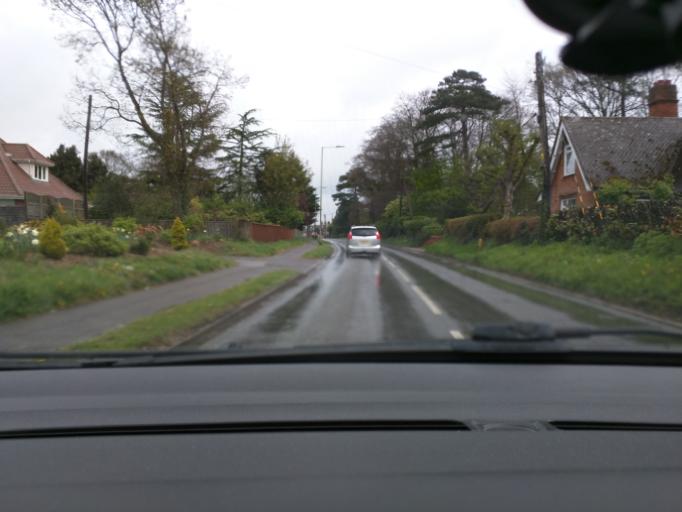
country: GB
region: England
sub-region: Suffolk
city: Leiston
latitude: 52.2009
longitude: 1.5716
